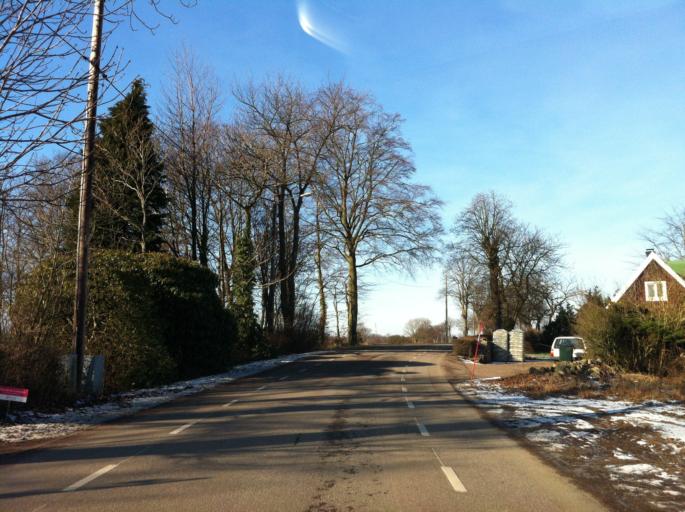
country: SE
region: Skane
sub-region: Angelholms Kommun
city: Strovelstorp
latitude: 56.1085
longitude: 12.7904
